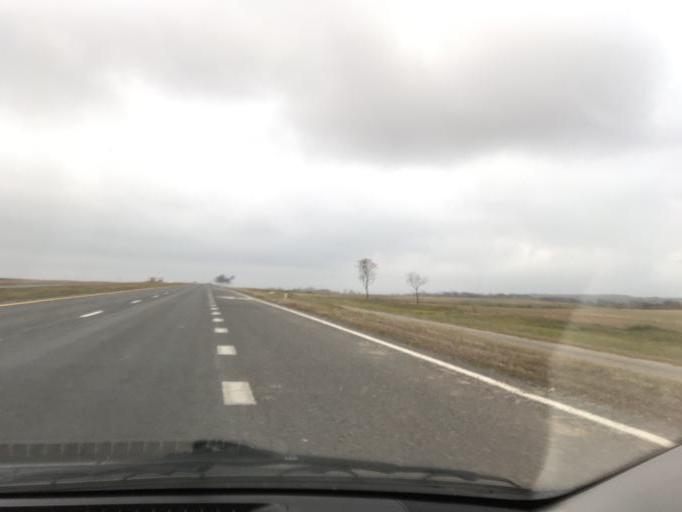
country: BY
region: Vitebsk
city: Vitebsk
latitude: 55.1526
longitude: 30.1063
